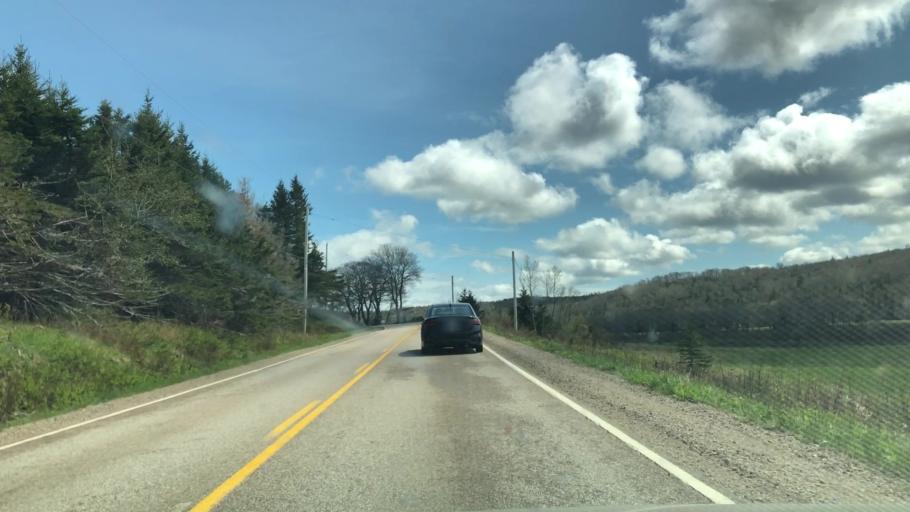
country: CA
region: Nova Scotia
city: Antigonish
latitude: 45.2028
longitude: -62.0036
